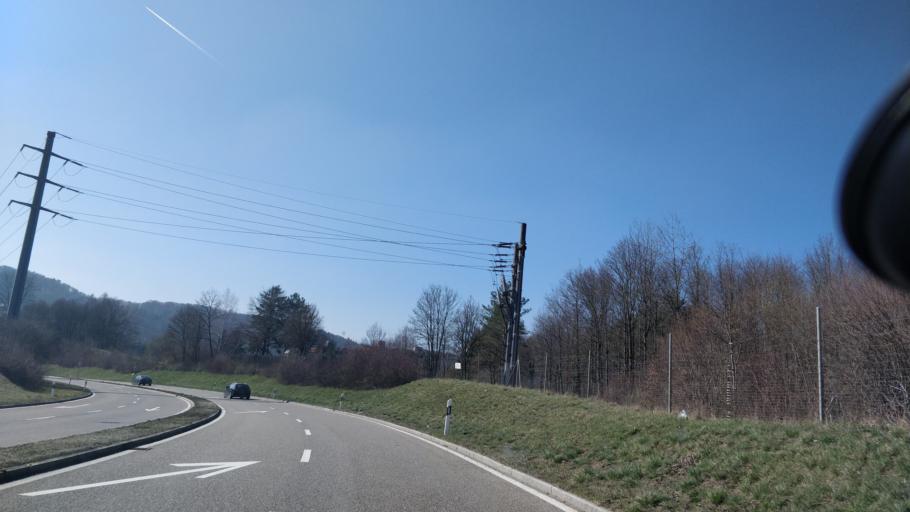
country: CH
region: Zurich
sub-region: Bezirk Buelach
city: Embrach / Kellersacker
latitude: 47.5234
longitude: 8.5924
